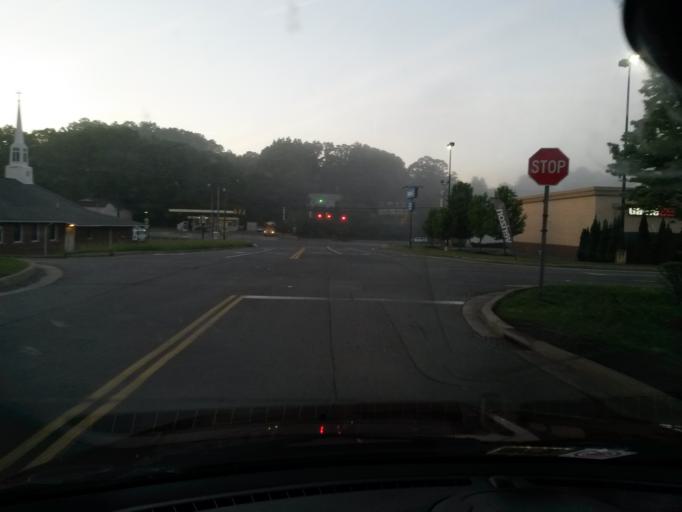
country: US
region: West Virginia
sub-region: Raleigh County
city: MacArthur
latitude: 37.7539
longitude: -81.2197
